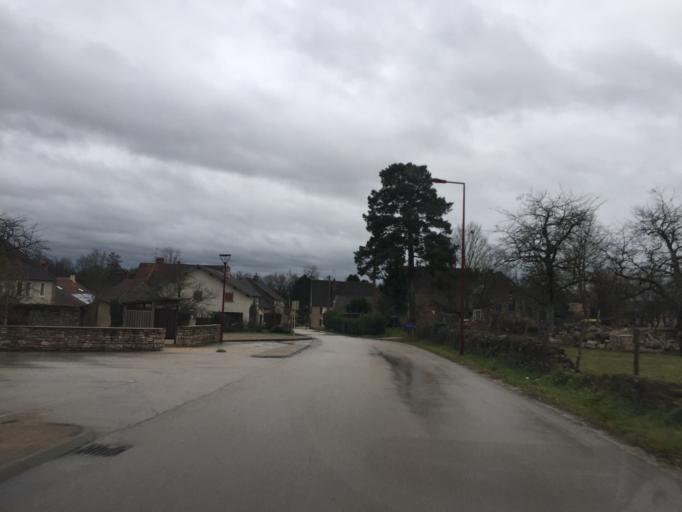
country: FR
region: Franche-Comte
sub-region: Departement du Jura
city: Champvans
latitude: 47.1470
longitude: 5.4591
